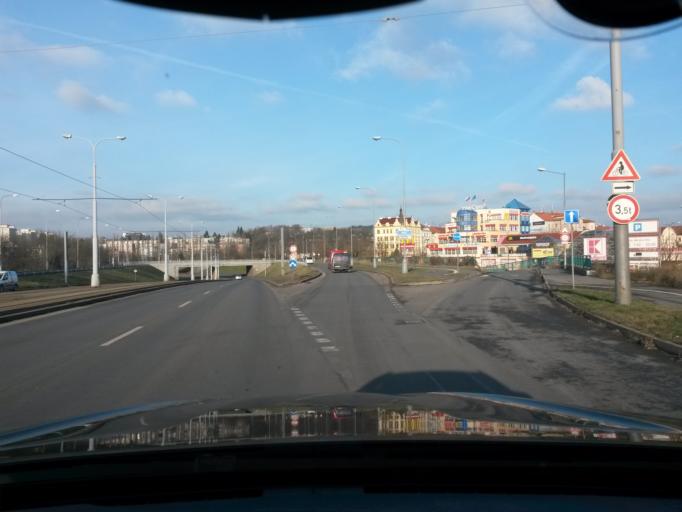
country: CZ
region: Plzensky
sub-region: Okres Plzen-Mesto
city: Pilsen
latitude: 49.7521
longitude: 13.3753
